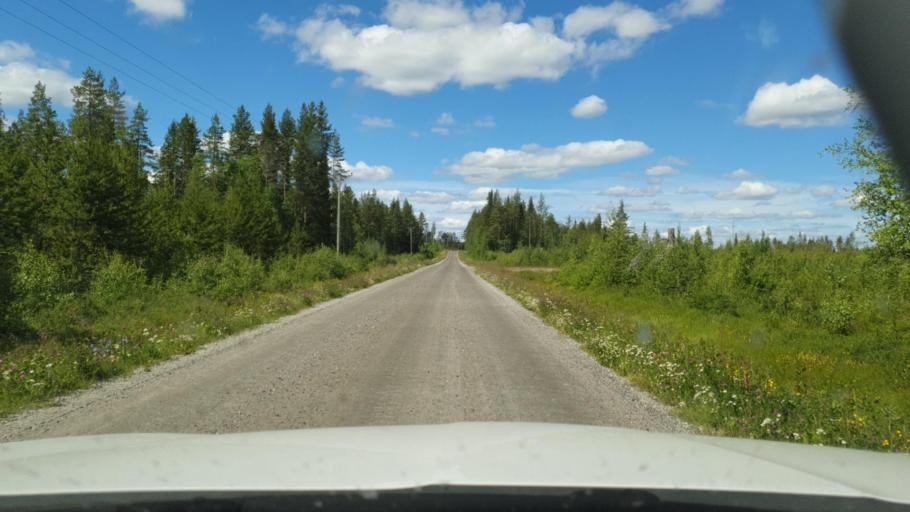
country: SE
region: Vaesterbotten
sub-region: Skelleftea Kommun
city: Backa
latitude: 65.1754
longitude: 21.0918
